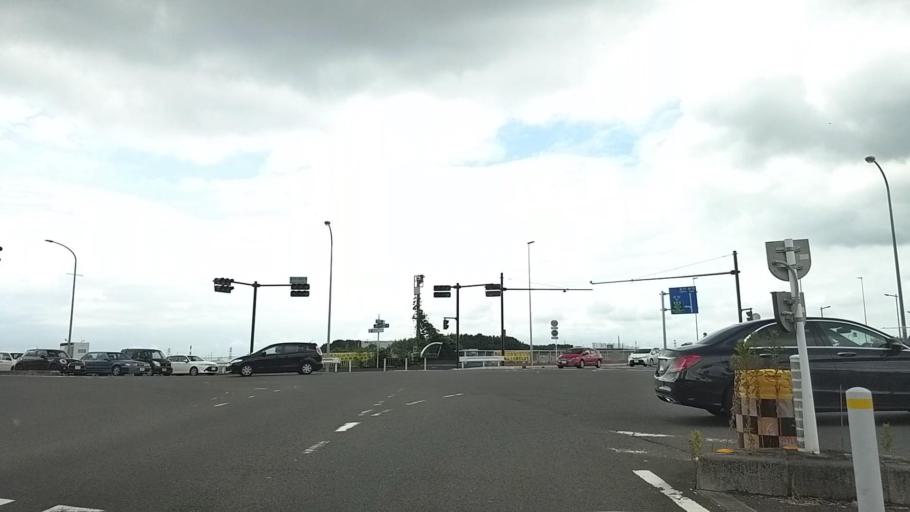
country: JP
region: Kanagawa
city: Yokohama
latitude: 35.5125
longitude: 139.6134
